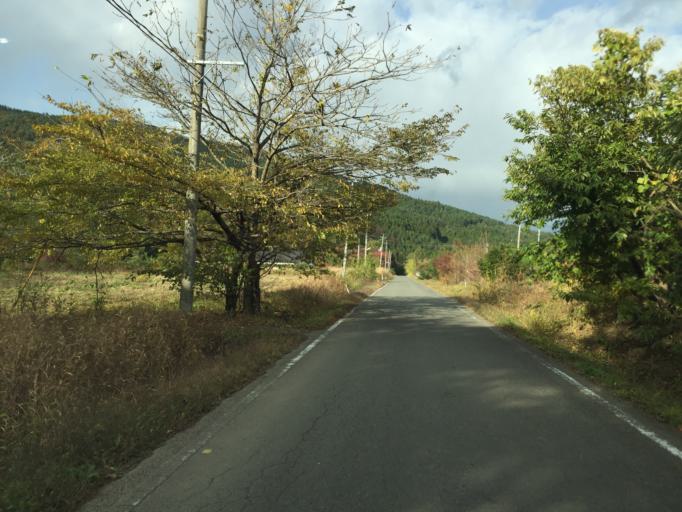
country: JP
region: Fukushima
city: Fukushima-shi
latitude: 37.7116
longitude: 140.3420
